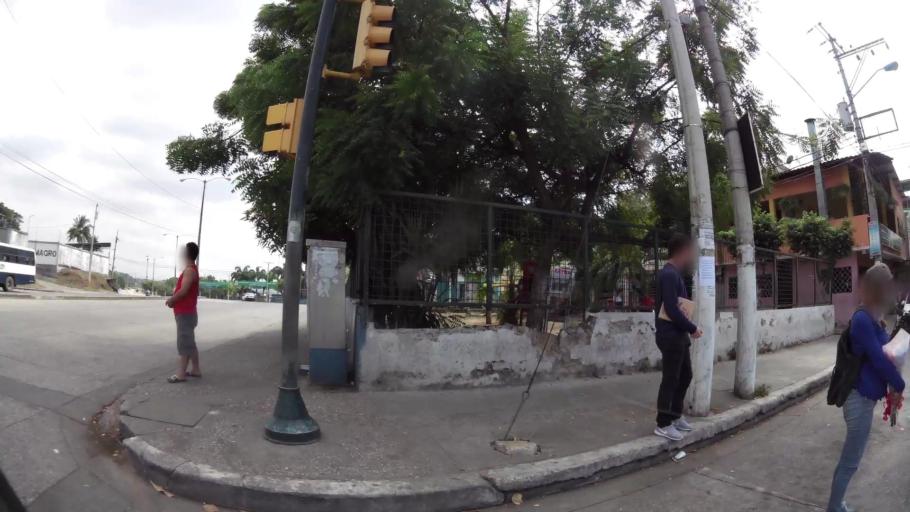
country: EC
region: Guayas
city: Santa Lucia
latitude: -2.0916
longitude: -79.9411
